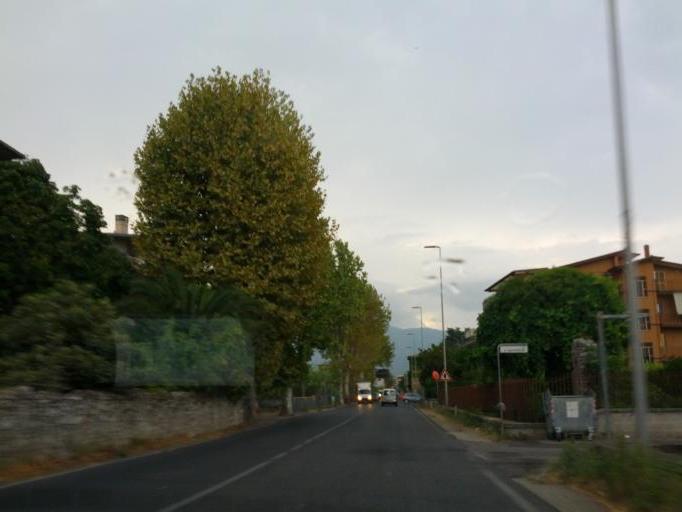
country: IT
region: Latium
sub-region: Provincia di Latina
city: Fondi
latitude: 41.3482
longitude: 13.4413
